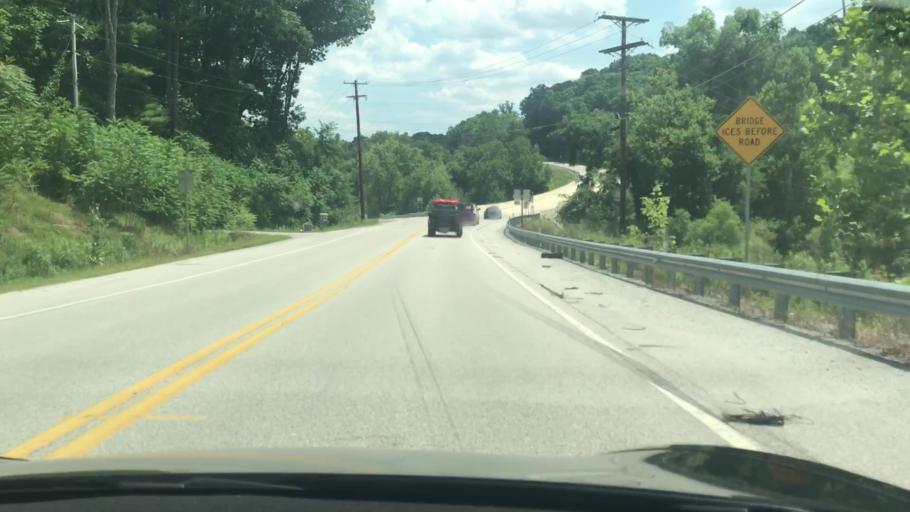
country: US
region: Pennsylvania
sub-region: York County
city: Manchester
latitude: 40.1013
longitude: -76.7651
